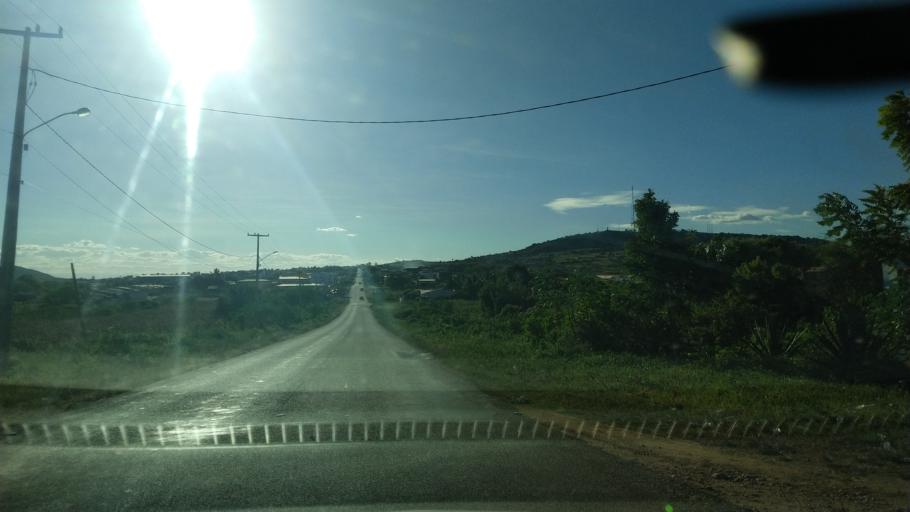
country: BR
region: Rio Grande do Norte
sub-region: Sao Jose Do Campestre
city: Sao Jose do Campestre
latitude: -6.3224
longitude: -35.7030
